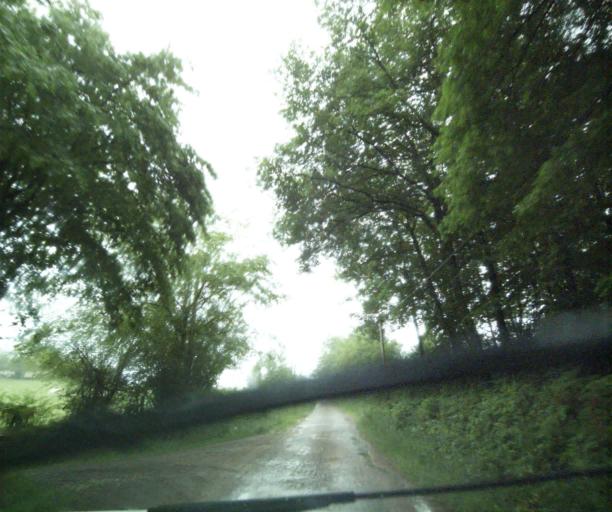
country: FR
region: Bourgogne
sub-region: Departement de Saone-et-Loire
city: Charolles
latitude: 46.3762
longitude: 4.3452
